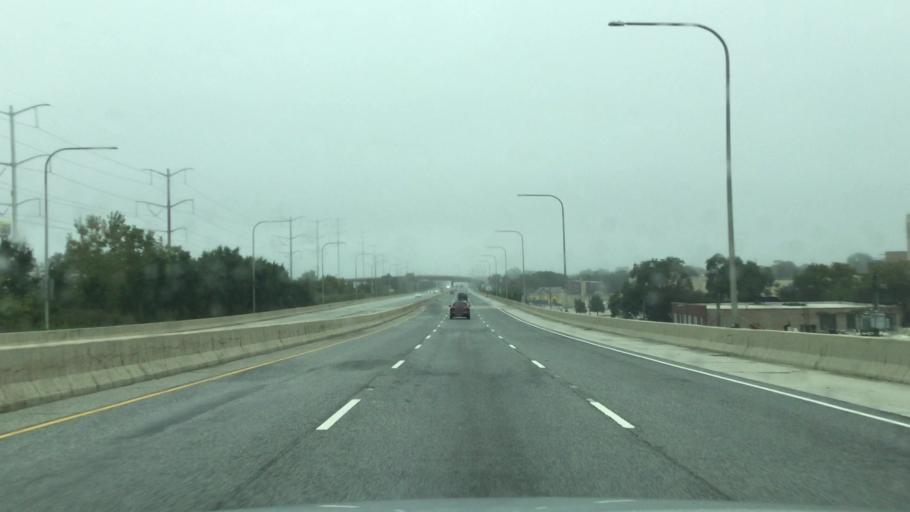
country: US
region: Illinois
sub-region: Cook County
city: Chicago
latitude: 41.7546
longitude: -87.5925
